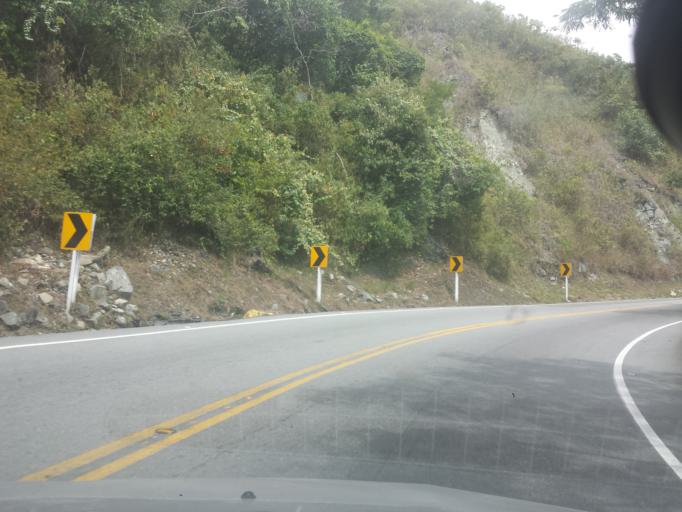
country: CO
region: Antioquia
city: Antioquia
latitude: 6.6117
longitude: -75.8506
